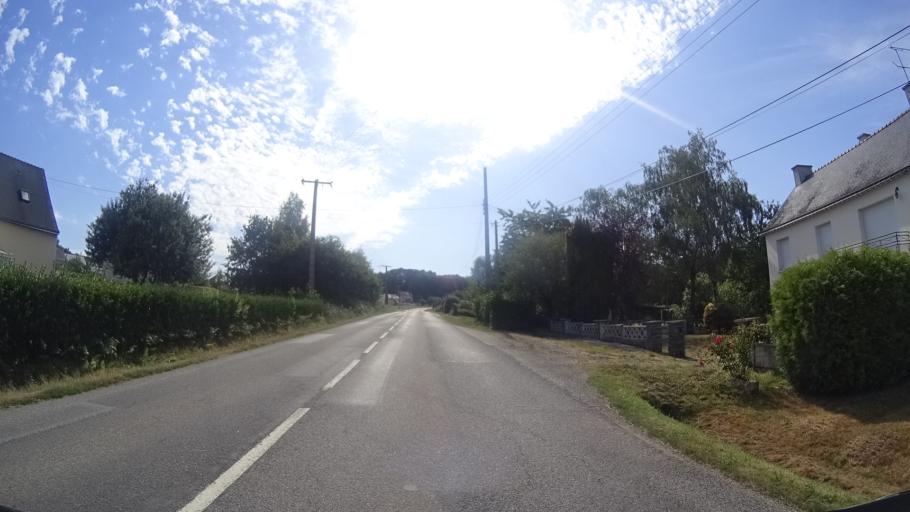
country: FR
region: Brittany
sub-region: Departement du Morbihan
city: Beganne
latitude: 47.5977
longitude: -2.2471
